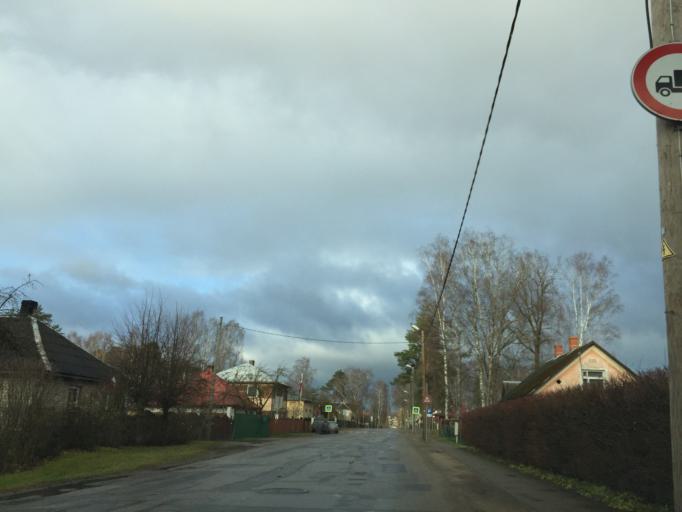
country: LV
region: Valmieras Rajons
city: Valmiera
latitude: 57.5247
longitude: 25.4296
